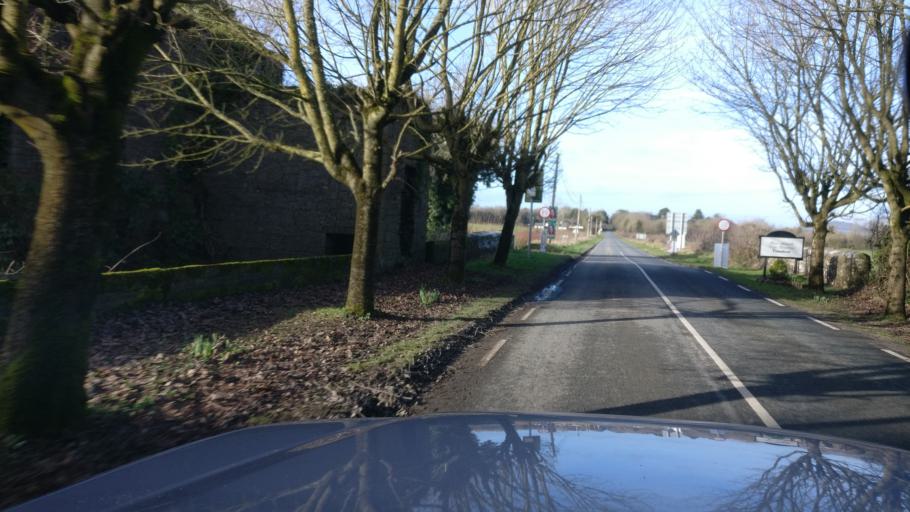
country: IE
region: Leinster
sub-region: Laois
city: Stradbally
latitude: 52.9624
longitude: -7.2027
